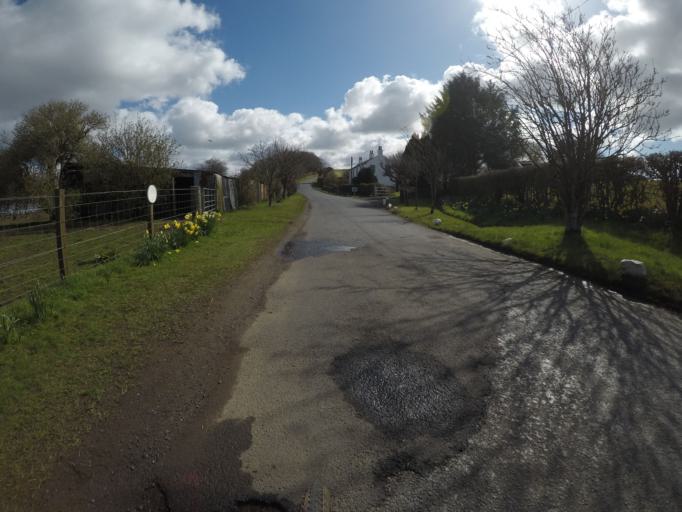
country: GB
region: Scotland
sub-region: East Ayrshire
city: Crosshouse
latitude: 55.5918
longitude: -4.5530
